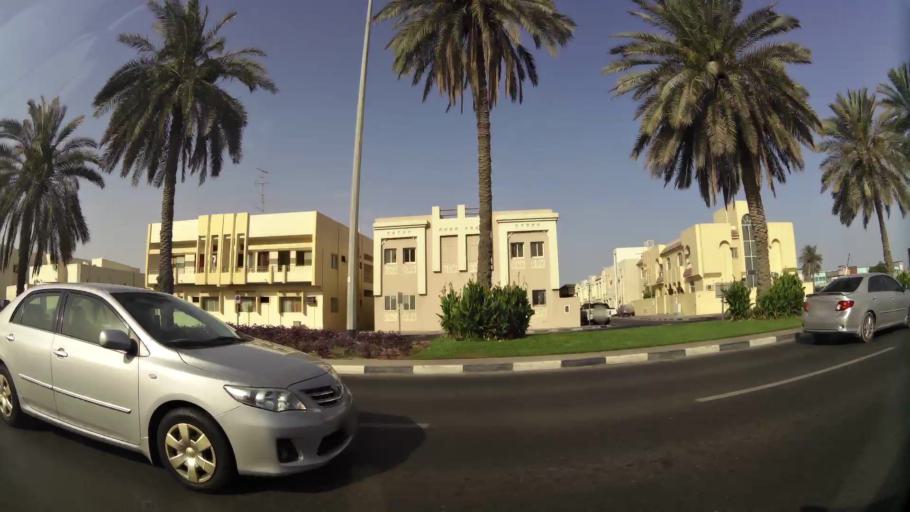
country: AE
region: Ash Shariqah
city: Sharjah
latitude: 25.2921
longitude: 55.3284
